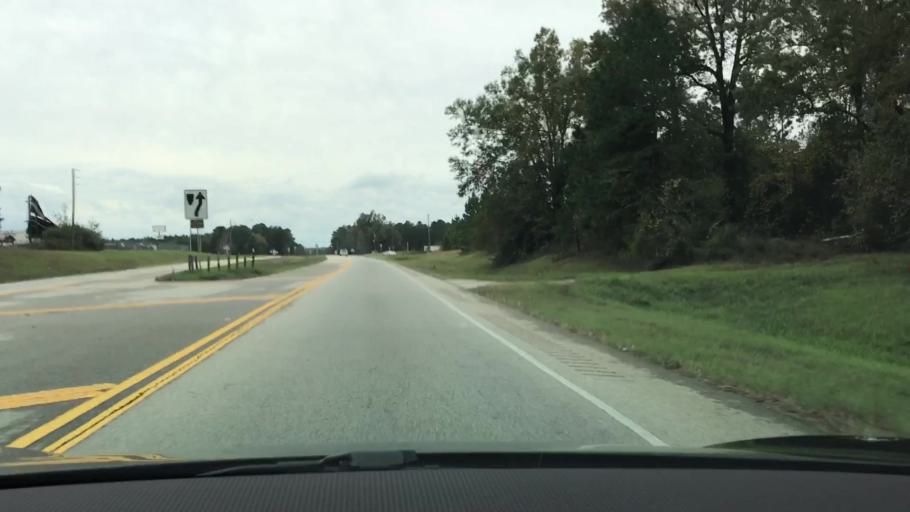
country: US
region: Georgia
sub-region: Jefferson County
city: Louisville
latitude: 32.9876
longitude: -82.3927
